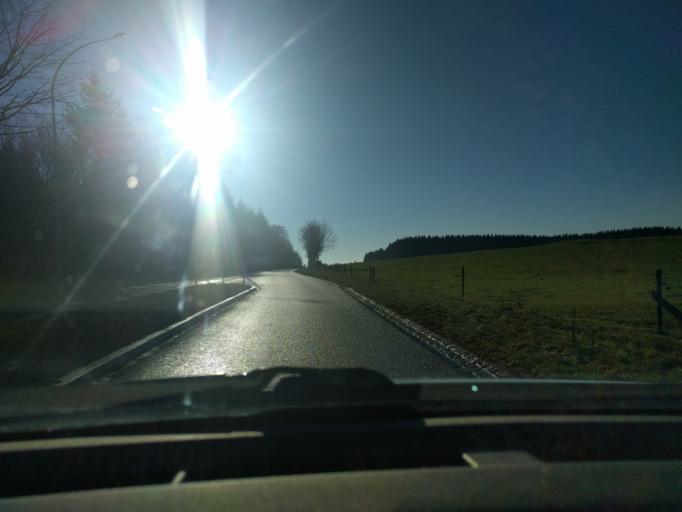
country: LU
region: Diekirch
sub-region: Canton de Clervaux
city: Troisvierges
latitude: 50.1793
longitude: 6.0248
